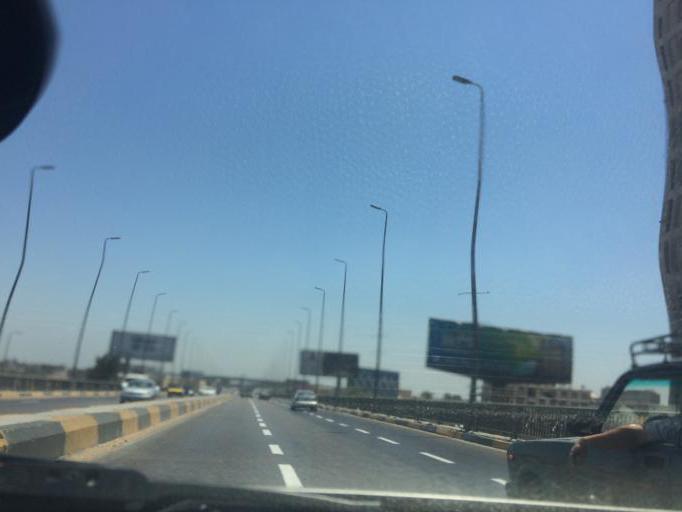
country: EG
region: Alexandria
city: Alexandria
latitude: 31.1869
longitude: 29.9247
